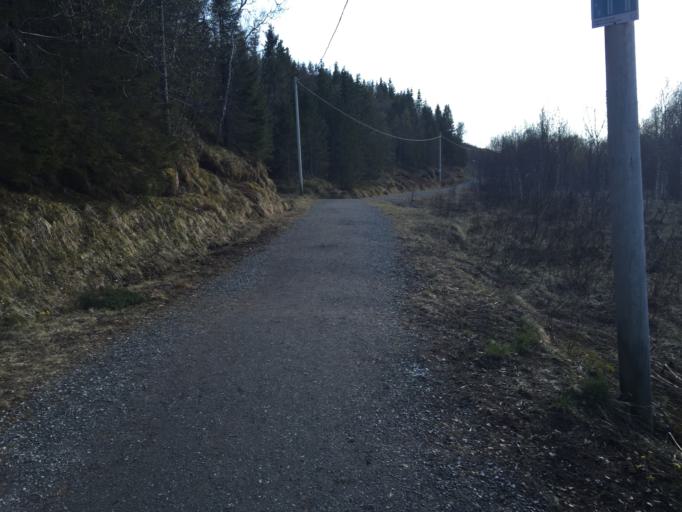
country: NO
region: Nordland
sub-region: Bodo
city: Lopsmarka
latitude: 67.2919
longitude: 14.5465
